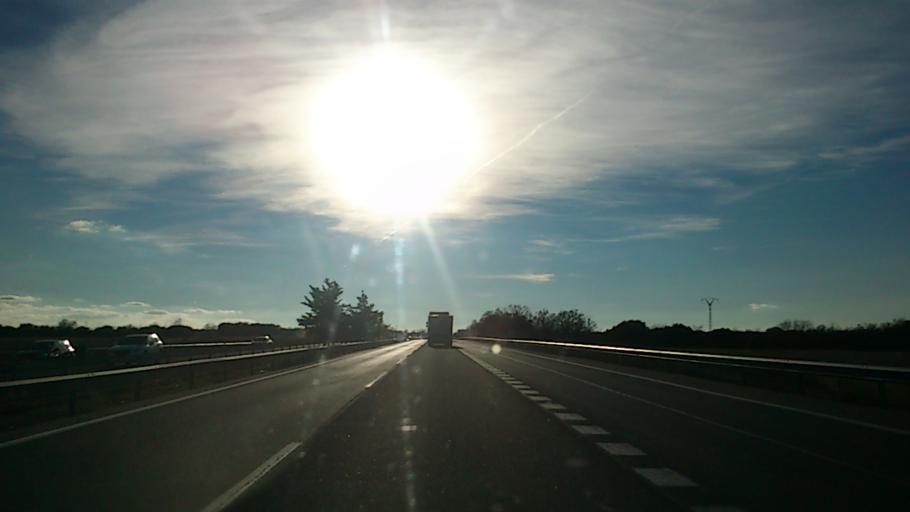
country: ES
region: Castille-La Mancha
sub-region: Provincia de Guadalajara
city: Almadrones
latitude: 40.9109
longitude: -2.7404
